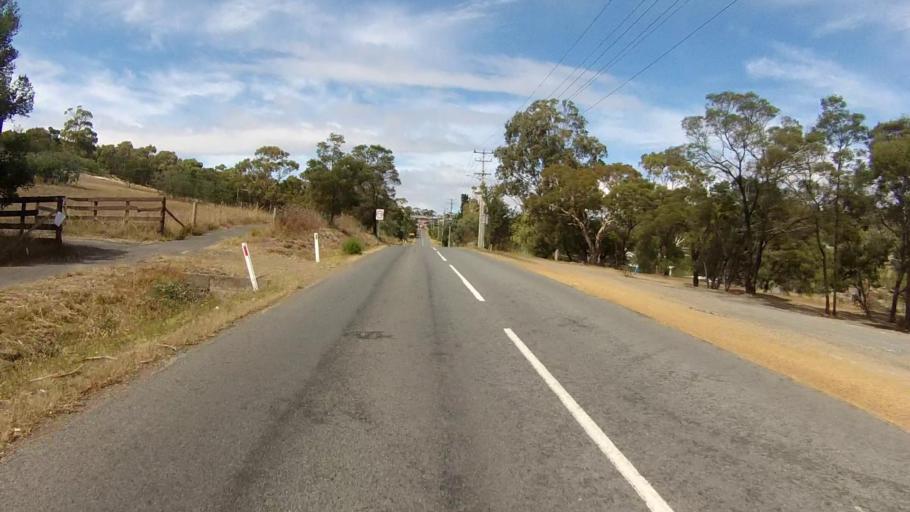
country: AU
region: Tasmania
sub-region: Clarence
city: Lindisfarne
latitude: -42.8162
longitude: 147.3513
